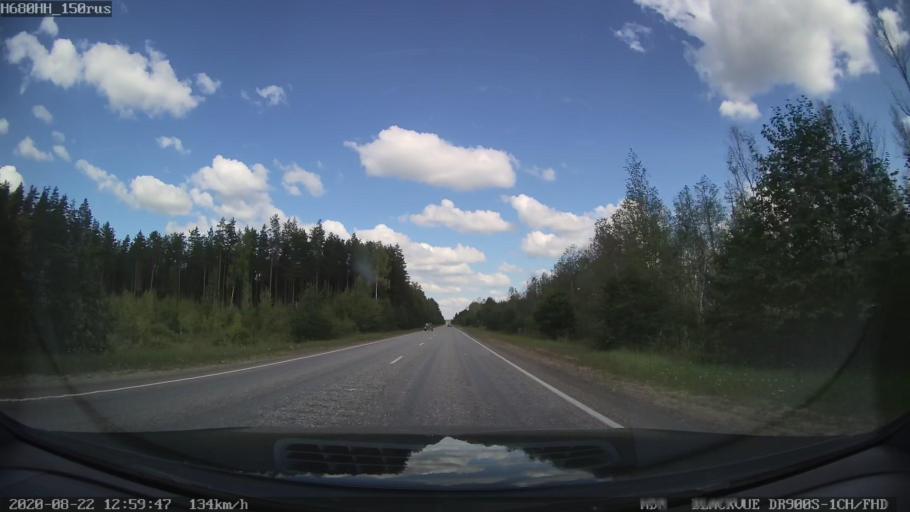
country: RU
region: Tverskaya
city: Bezhetsk
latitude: 57.6120
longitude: 36.3652
